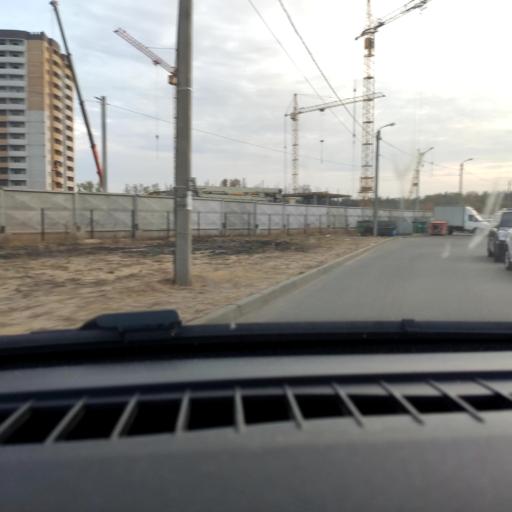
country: RU
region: Voronezj
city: Podgornoye
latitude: 51.7321
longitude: 39.1830
